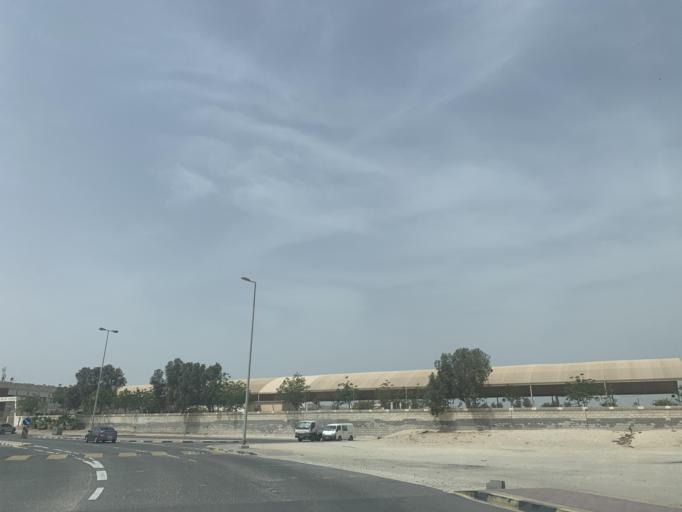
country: BH
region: Northern
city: Madinat `Isa
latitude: 26.1593
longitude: 50.5403
